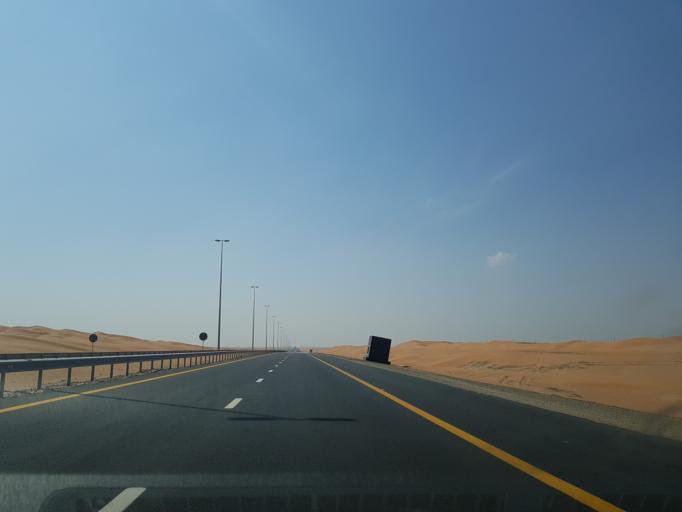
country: AE
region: Ash Shariqah
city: Adh Dhayd
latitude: 25.2497
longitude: 55.8051
